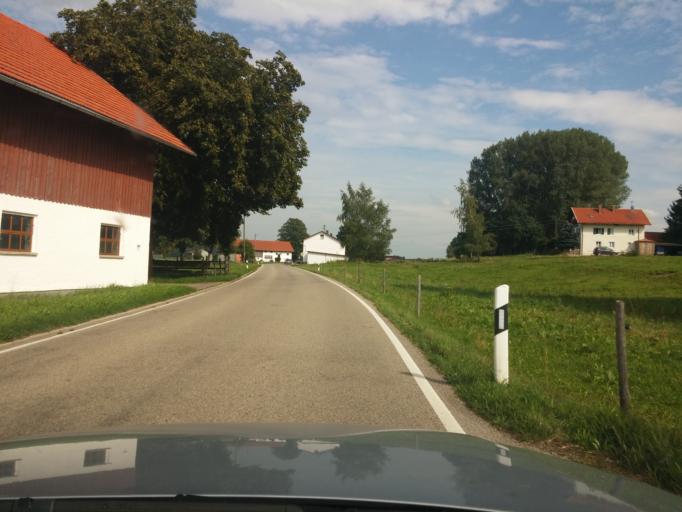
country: DE
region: Bavaria
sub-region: Swabia
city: Legau
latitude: 47.8467
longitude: 10.1498
